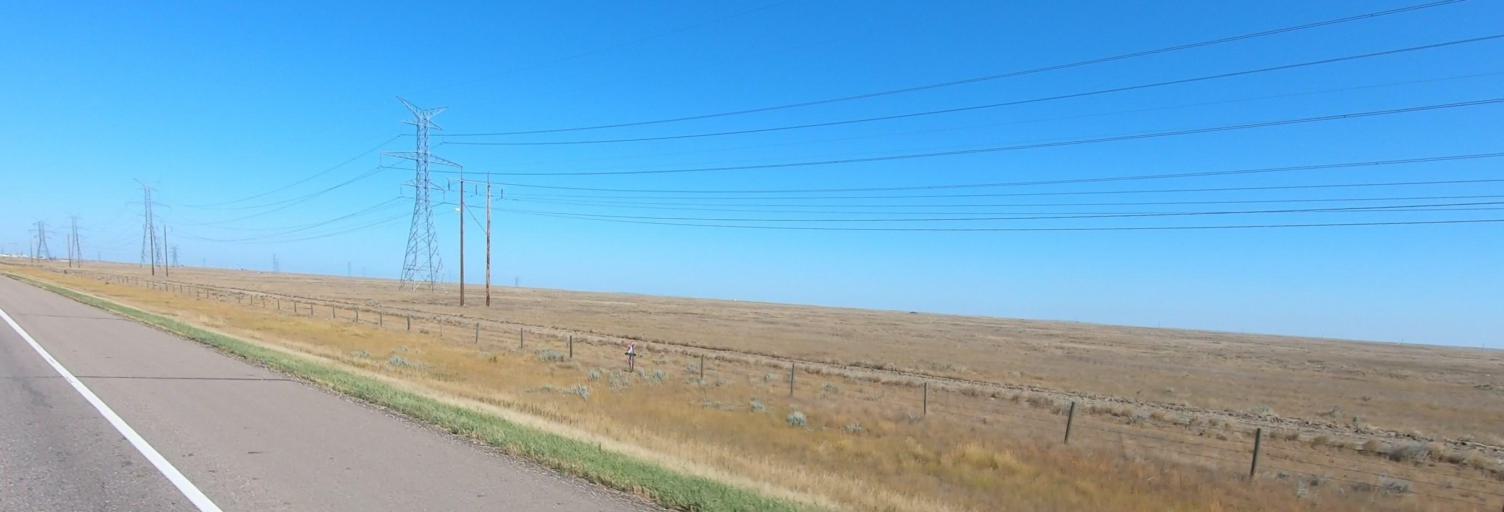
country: CA
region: Alberta
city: Brooks
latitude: 50.4468
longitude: -111.5669
